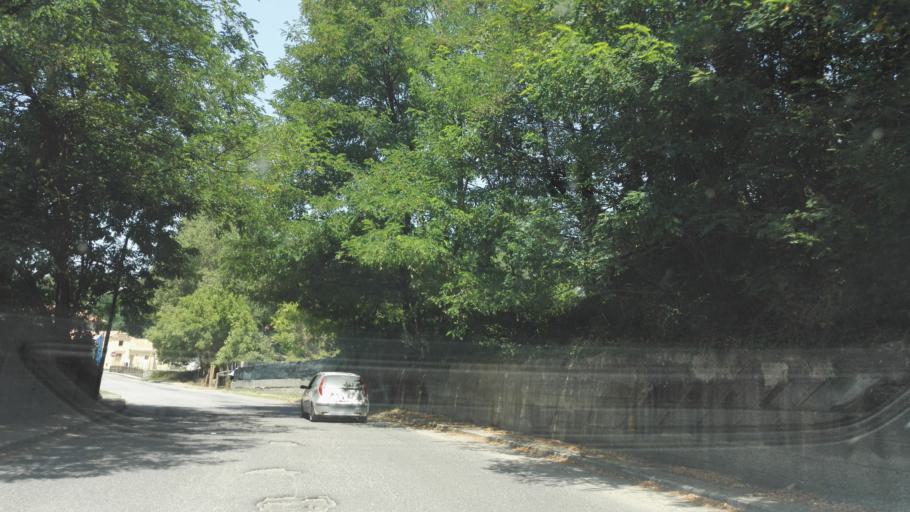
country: IT
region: Calabria
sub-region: Provincia di Vibo-Valentia
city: Serra San Bruno
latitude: 38.5805
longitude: 16.3341
